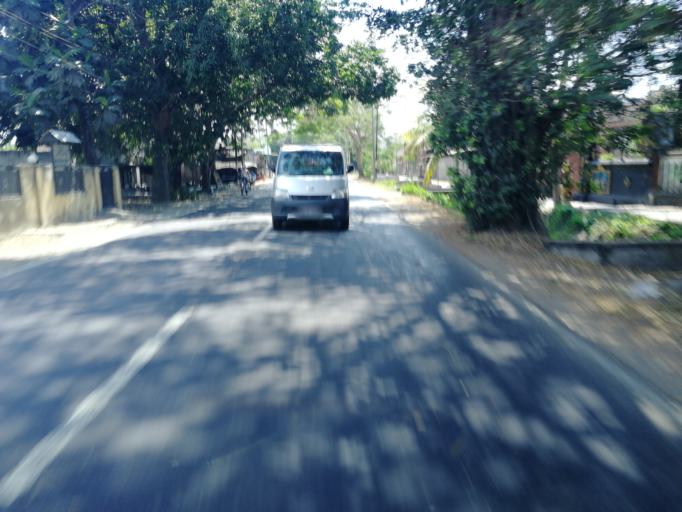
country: ID
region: West Nusa Tenggara
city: Jelateng Timur
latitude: -8.7012
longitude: 116.0990
